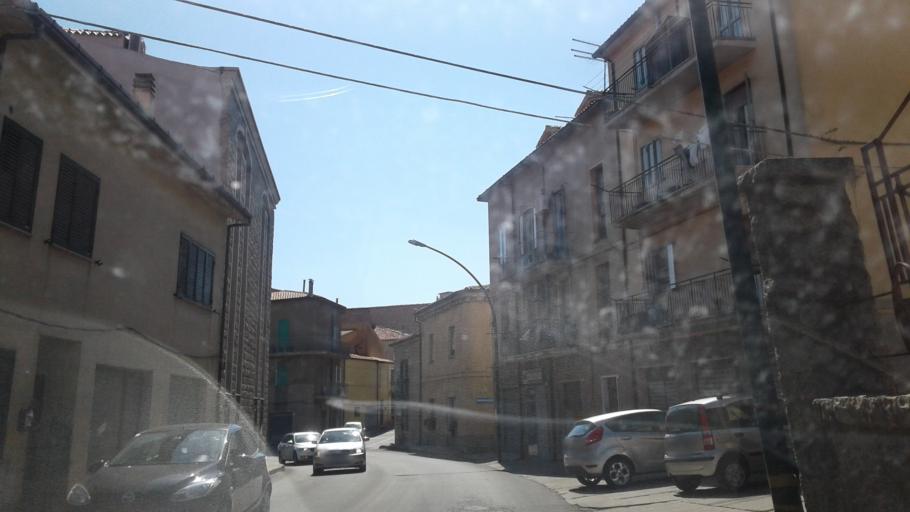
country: IT
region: Sardinia
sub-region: Provincia di Olbia-Tempio
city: Tempio Pausania
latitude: 40.9028
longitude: 9.1064
